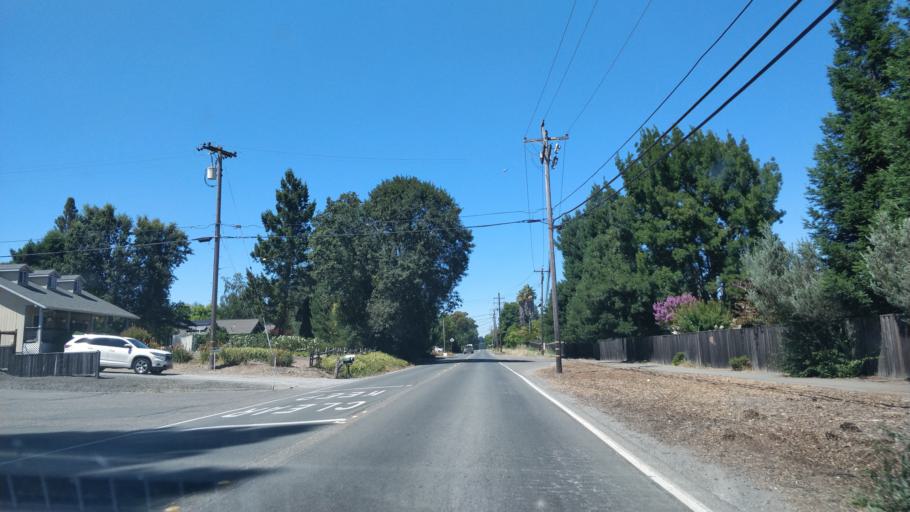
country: US
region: California
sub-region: Sonoma County
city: Forestville
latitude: 38.4752
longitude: -122.8948
